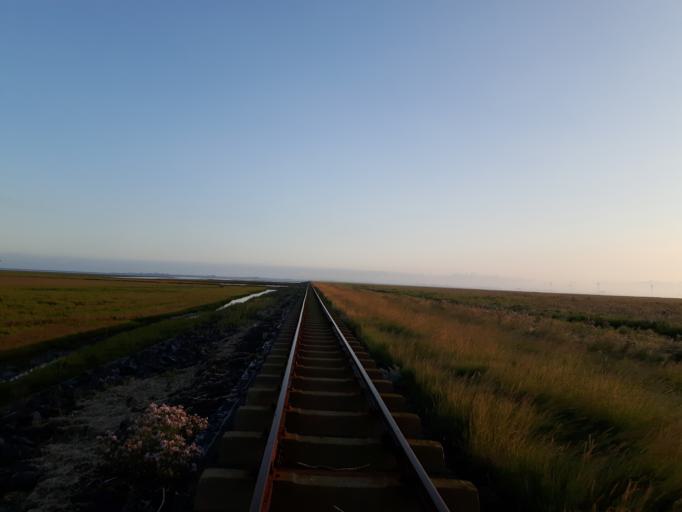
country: DE
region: Schleswig-Holstein
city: Dagebull
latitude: 54.6875
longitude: 8.7102
